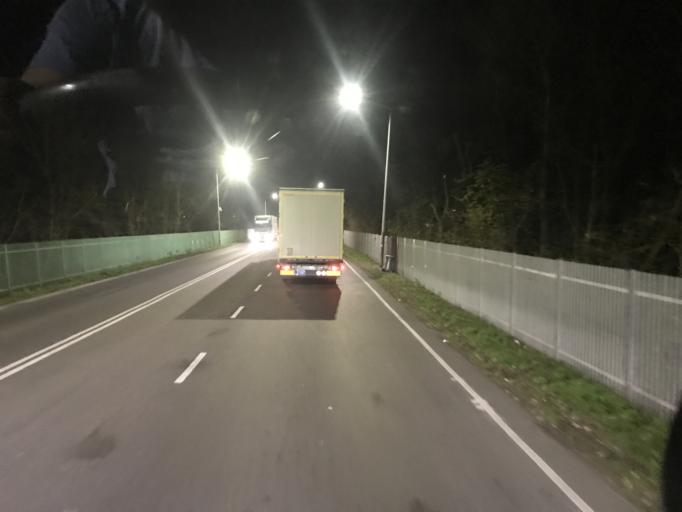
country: PL
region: Lublin Voivodeship
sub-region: Powiat bialski
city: Terespol
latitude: 52.1064
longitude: 23.5579
